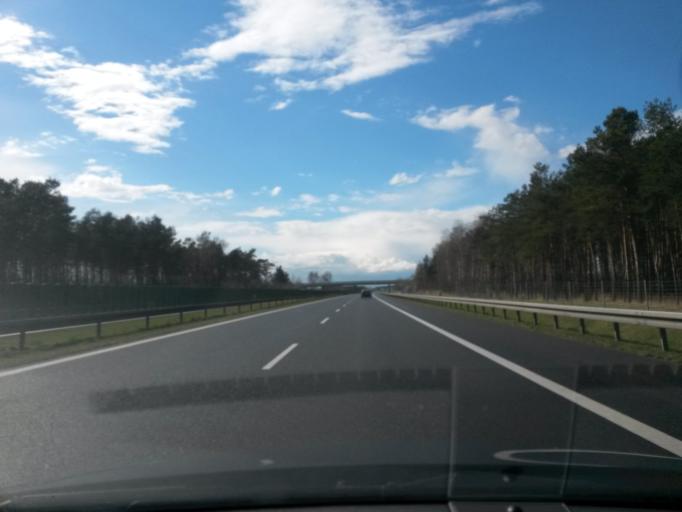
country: PL
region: Greater Poland Voivodeship
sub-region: Powiat slupecki
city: Strzalkowo
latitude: 52.2650
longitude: 17.7477
